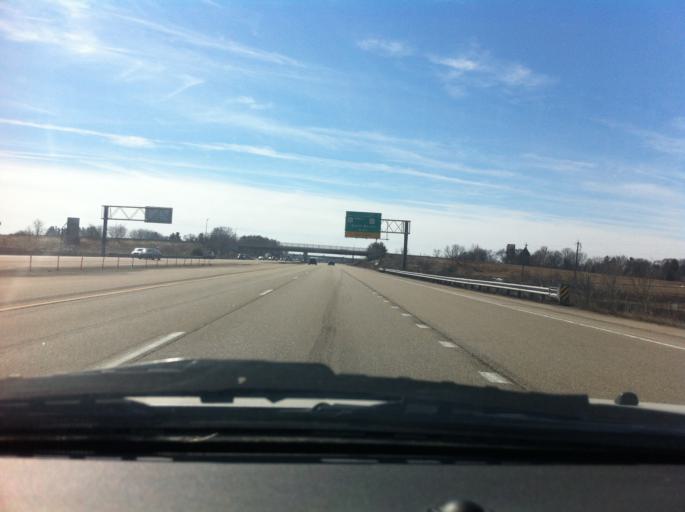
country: US
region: Wisconsin
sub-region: Rock County
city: Beloit
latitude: 42.5591
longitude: -88.9768
